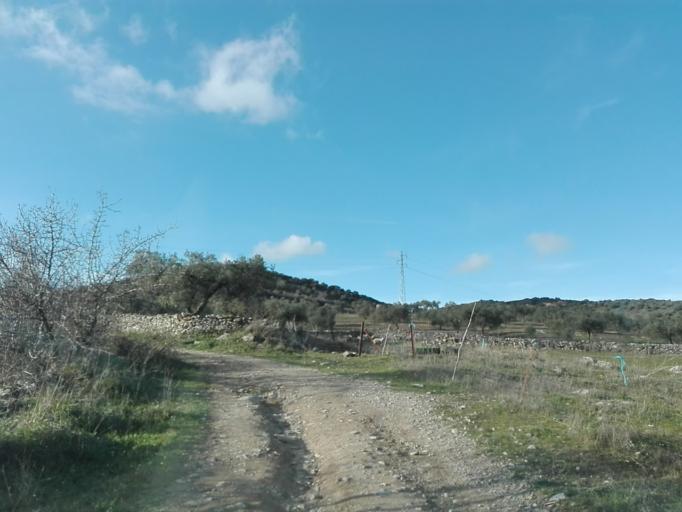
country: ES
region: Extremadura
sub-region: Provincia de Badajoz
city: Trasierra
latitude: 38.2017
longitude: -5.9961
